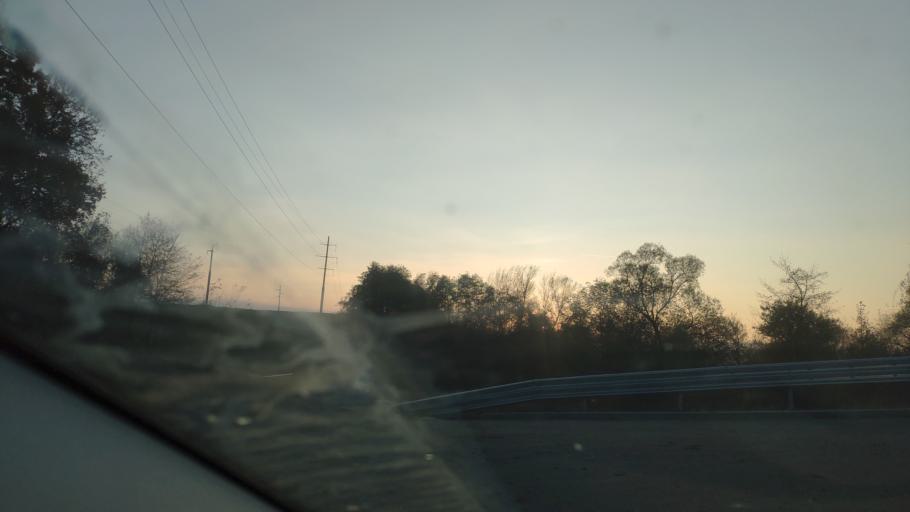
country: RO
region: Mures
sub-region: Comuna Chibed
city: Chibed
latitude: 46.5357
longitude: 24.9805
